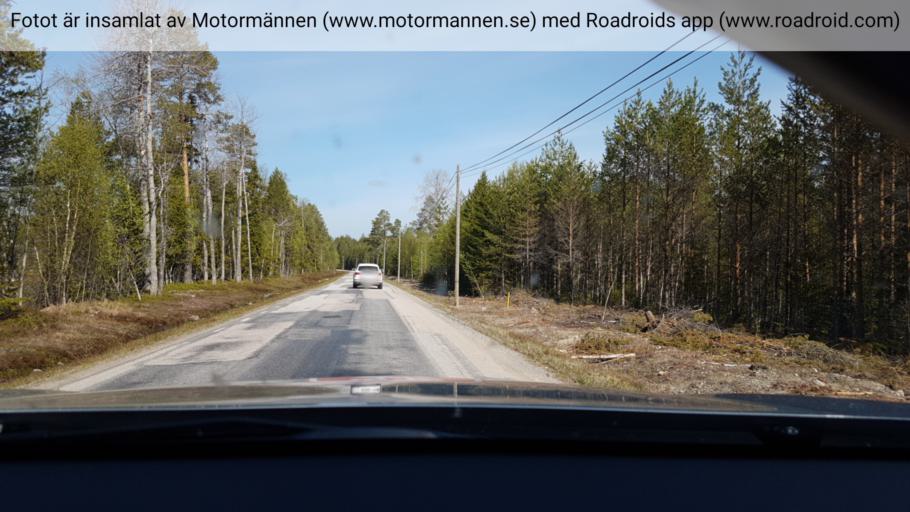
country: SE
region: Vaesterbotten
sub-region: Umea Kommun
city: Saevar
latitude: 63.8245
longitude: 20.5897
